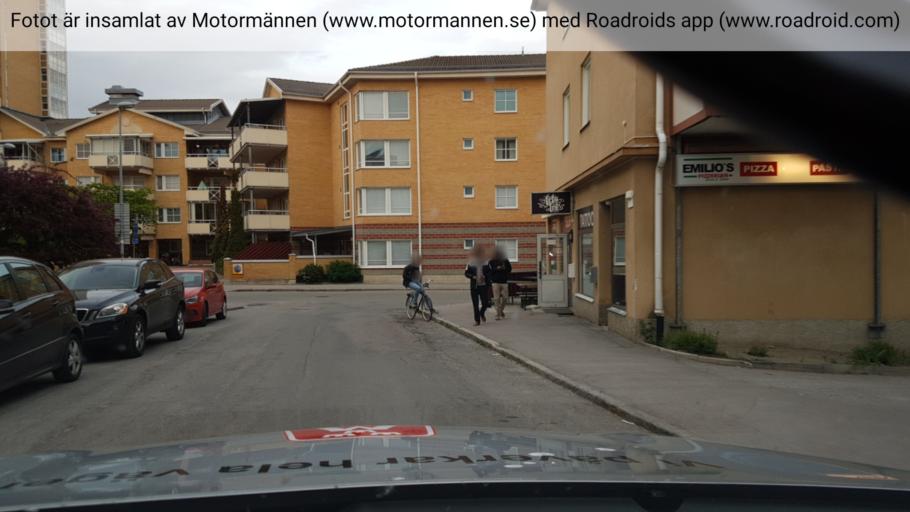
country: SE
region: Vaestmanland
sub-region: Vasteras
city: Vasteras
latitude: 59.6151
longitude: 16.5506
